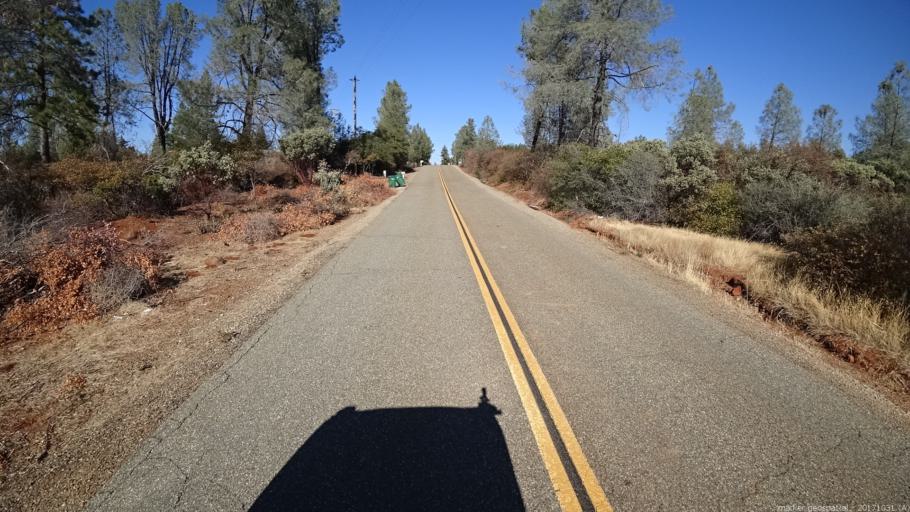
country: US
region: California
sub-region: Shasta County
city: Shingletown
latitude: 40.4996
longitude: -121.9950
